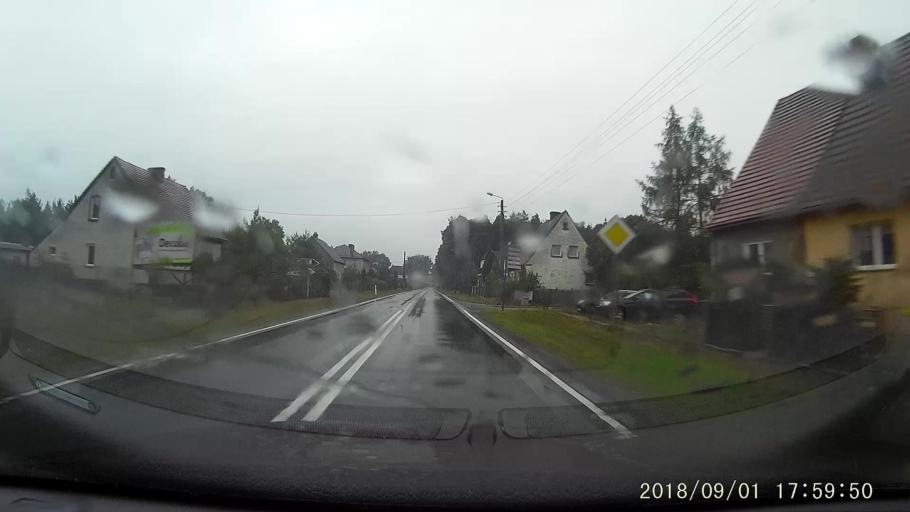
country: PL
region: Lubusz
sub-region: Powiat zaganski
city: Gozdnica
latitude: 51.4066
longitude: 15.1833
